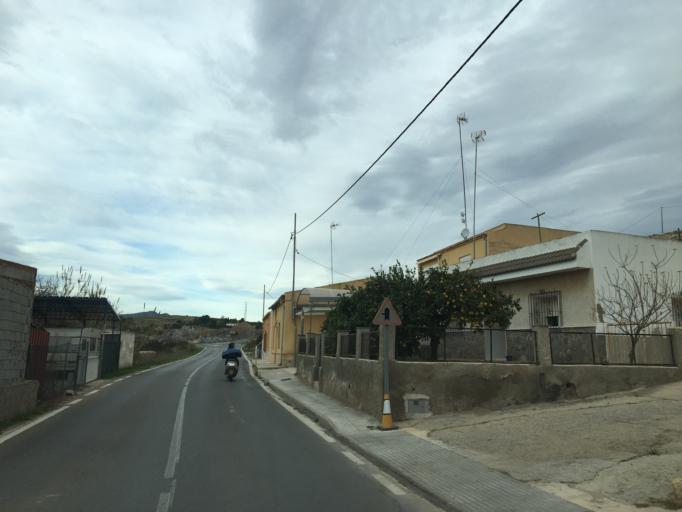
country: ES
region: Murcia
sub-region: Murcia
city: Cartagena
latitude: 37.6119
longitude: -1.0534
